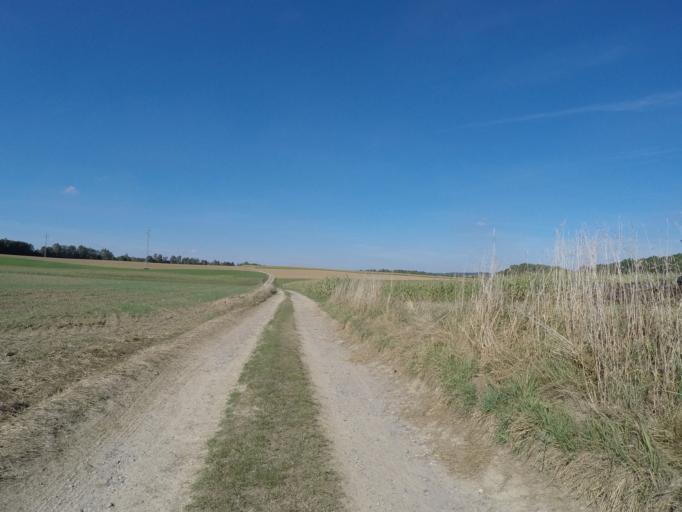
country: BE
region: Wallonia
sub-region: Province de Namur
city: Assesse
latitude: 50.3037
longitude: 5.0245
